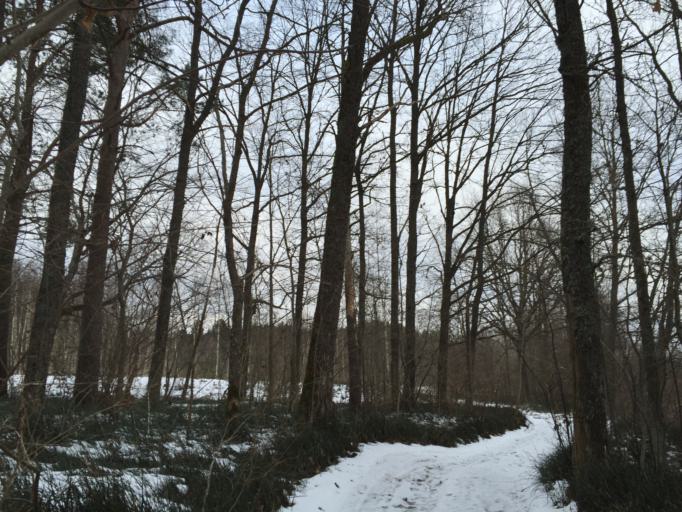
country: LV
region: Seja
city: Loja
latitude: 57.1297
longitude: 24.6639
